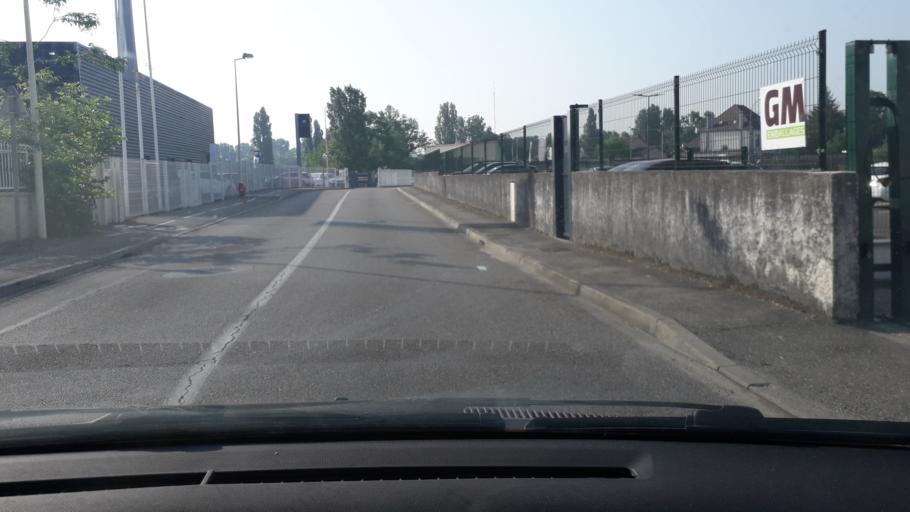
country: FR
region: Rhone-Alpes
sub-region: Departement de l'Isere
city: Charvieu-Chavagneux
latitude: 45.7494
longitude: 5.1667
